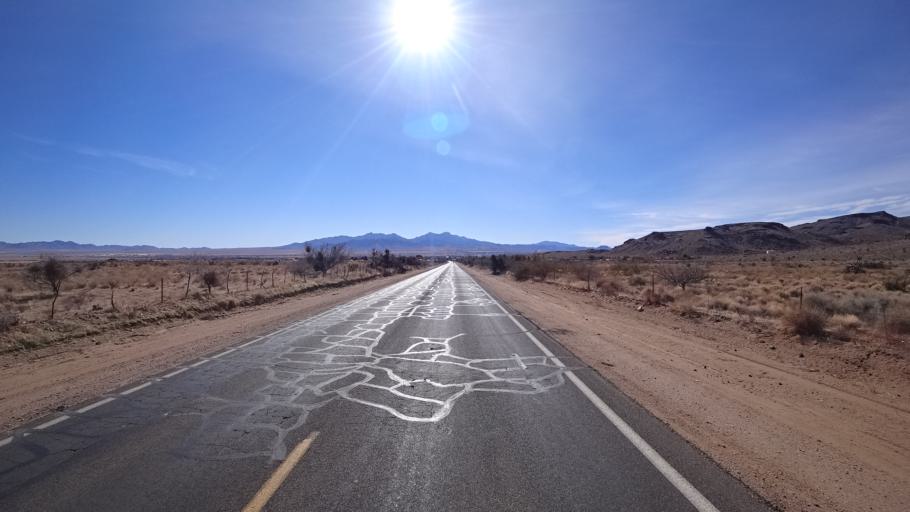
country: US
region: Arizona
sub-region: Mohave County
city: New Kingman-Butler
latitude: 35.2792
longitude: -114.0506
